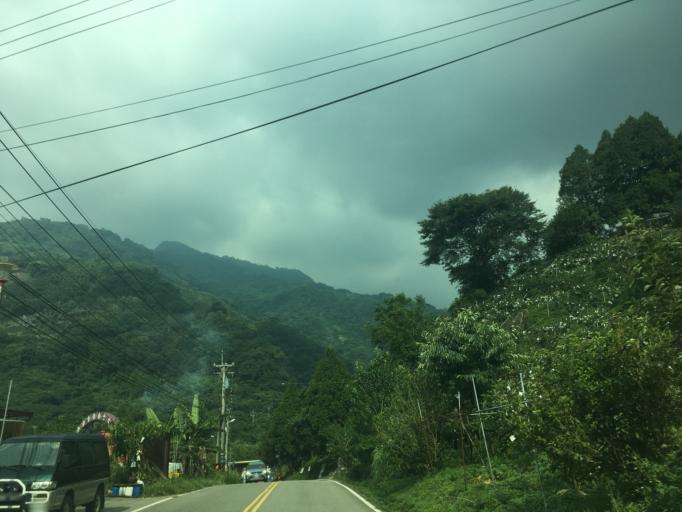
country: TW
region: Taiwan
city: Fengyuan
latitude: 24.3346
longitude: 120.9329
